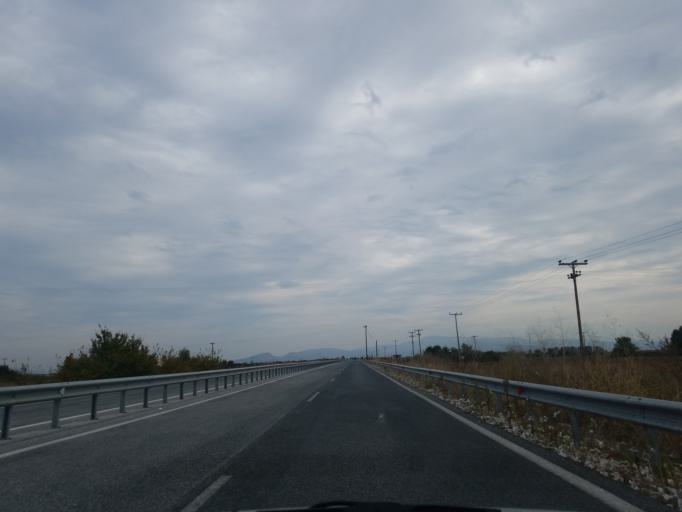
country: GR
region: Thessaly
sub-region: Nomos Kardhitsas
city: Sofades
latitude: 39.2947
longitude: 22.1649
